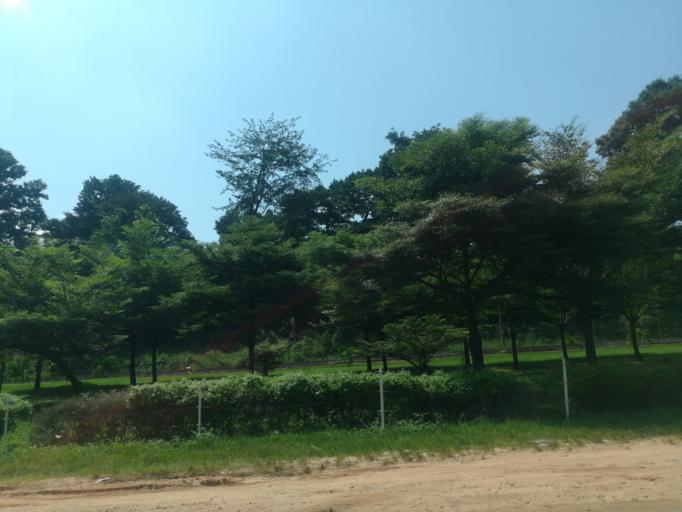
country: NG
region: Oyo
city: Moniya
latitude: 7.4944
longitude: 3.9147
